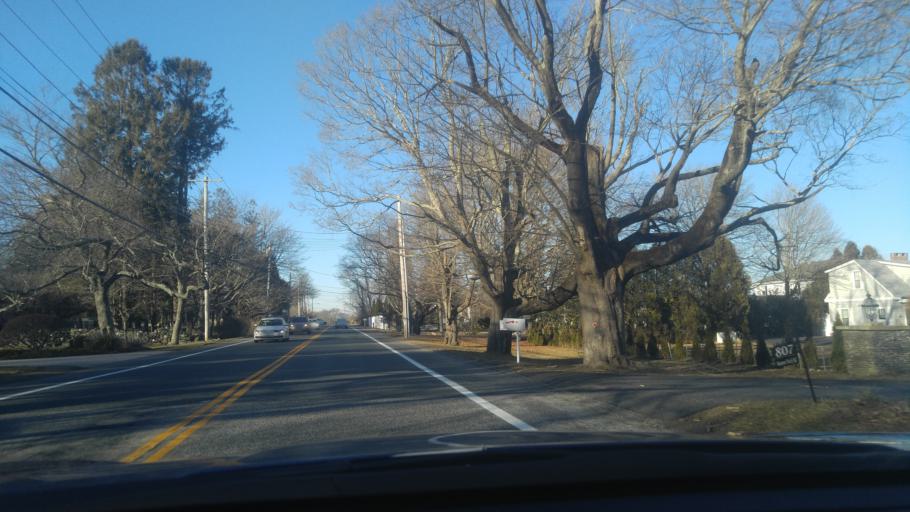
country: US
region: Rhode Island
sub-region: Washington County
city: Narragansett Pier
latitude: 41.4704
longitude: -71.4339
